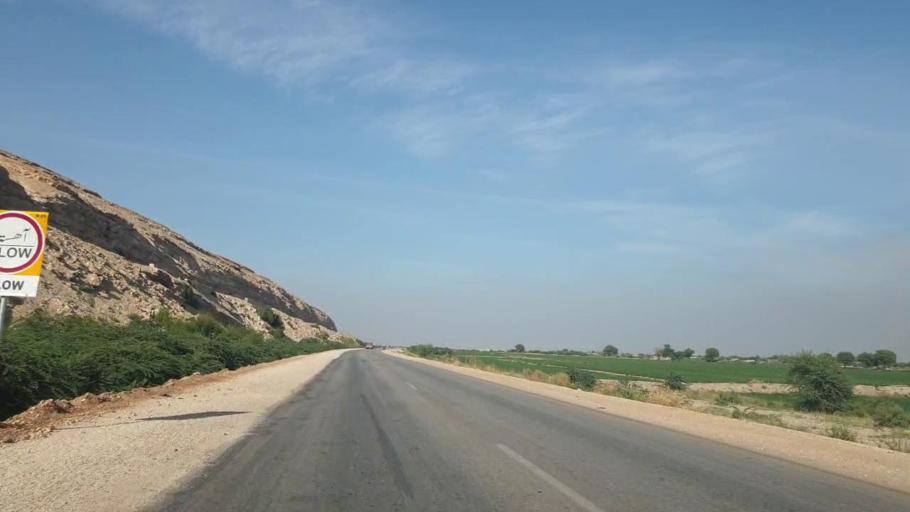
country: PK
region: Sindh
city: Sehwan
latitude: 26.3570
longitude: 67.8731
